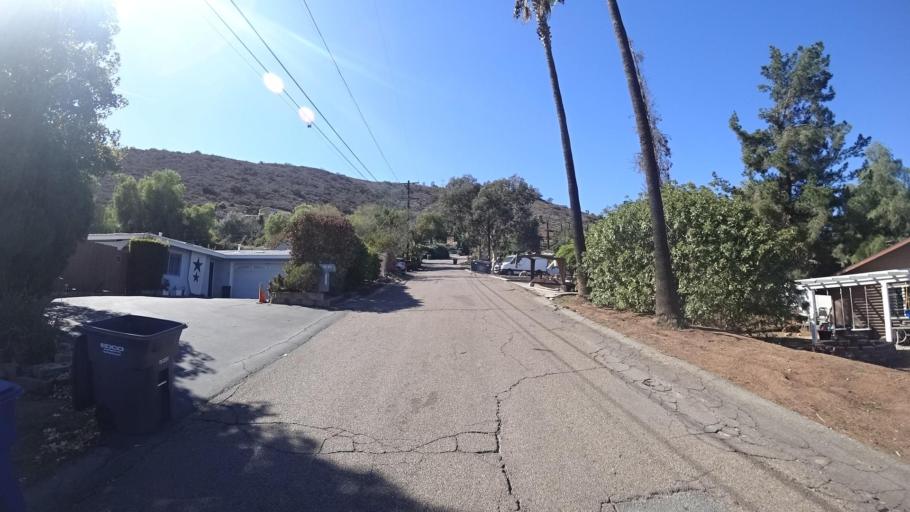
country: US
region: California
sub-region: San Diego County
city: Winter Gardens
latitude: 32.8280
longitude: -116.9364
